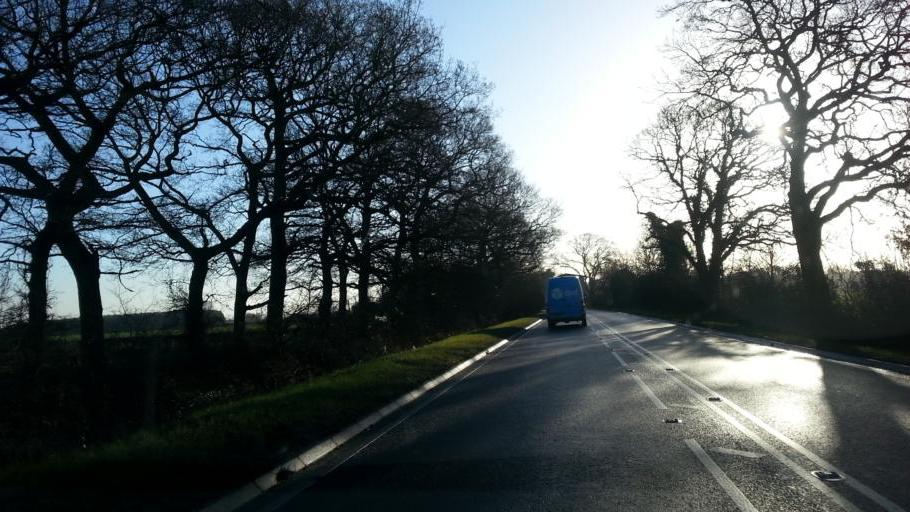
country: GB
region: England
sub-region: Nottinghamshire
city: South Collingham
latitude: 53.0819
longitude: -0.7251
